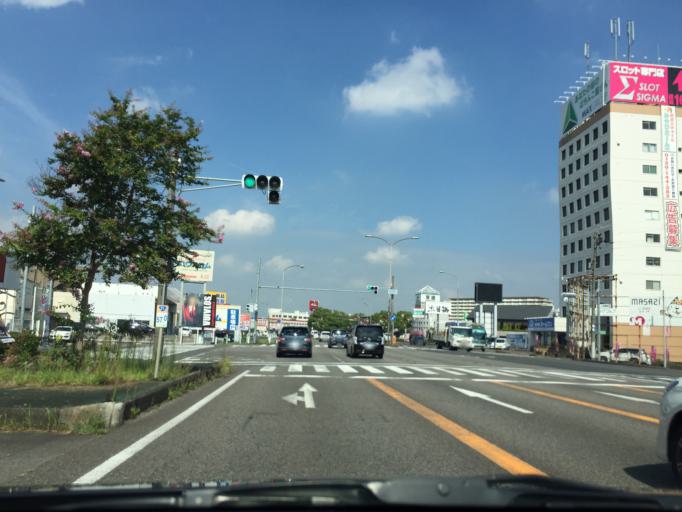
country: JP
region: Gifu
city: Gifu-shi
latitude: 35.3947
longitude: 136.7326
